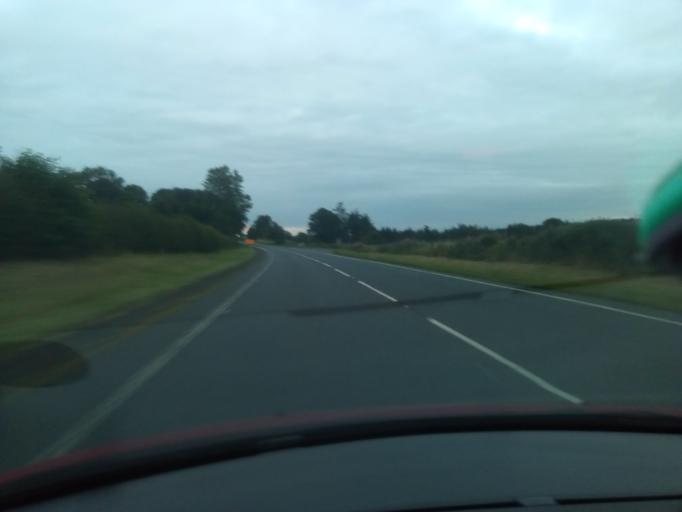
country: GB
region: England
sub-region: Northumberland
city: Bardon Mill
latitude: 54.9711
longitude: -2.2752
